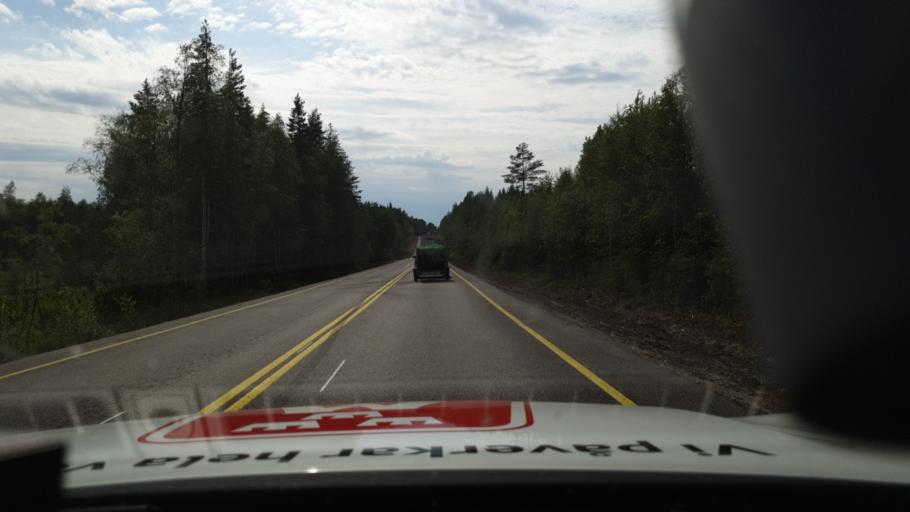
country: SE
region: Norrbotten
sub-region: Lulea Kommun
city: Ranea
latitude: 65.8670
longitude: 22.3213
